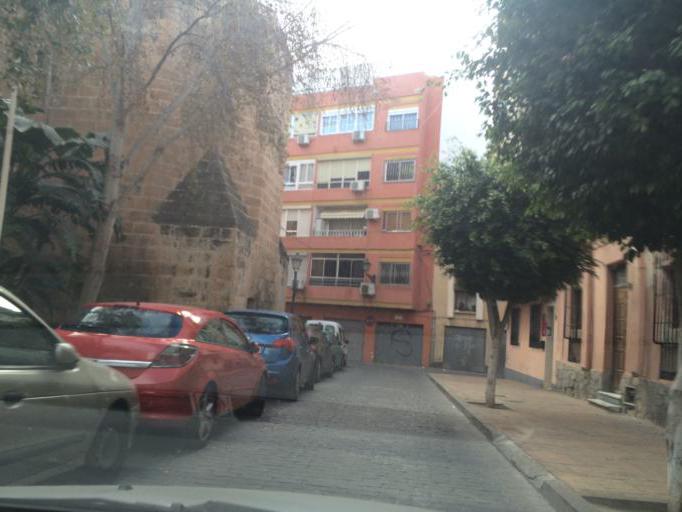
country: ES
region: Andalusia
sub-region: Provincia de Almeria
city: Almeria
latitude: 36.8381
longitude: -2.4679
